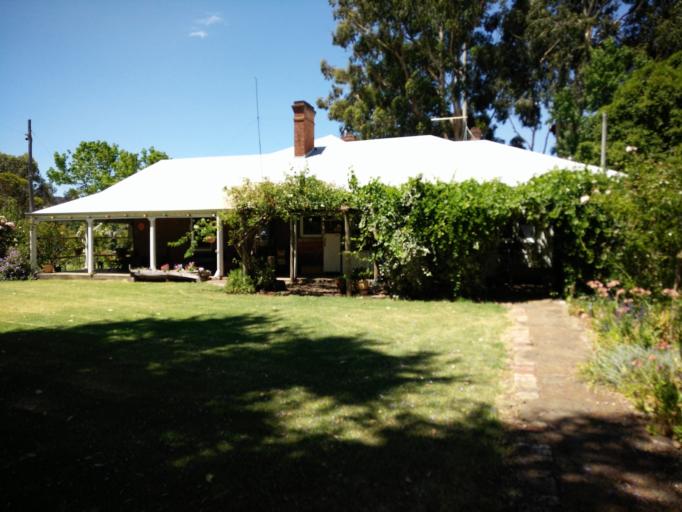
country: AU
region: Western Australia
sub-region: Bridgetown-Greenbushes
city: Bridgetown
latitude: -33.9368
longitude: 116.0255
